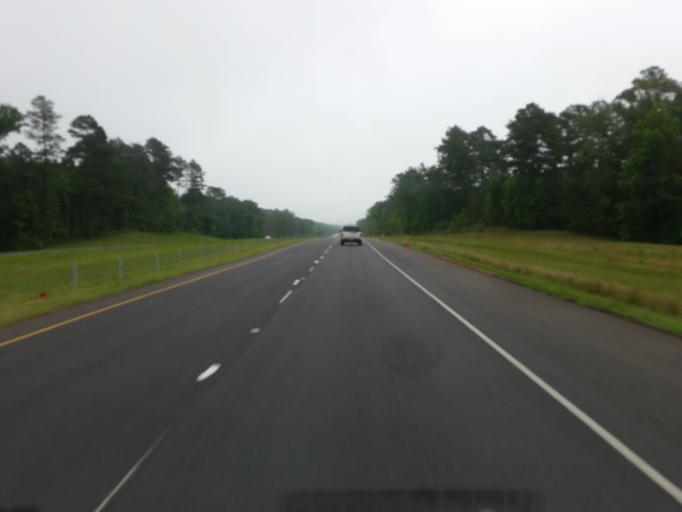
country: US
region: Louisiana
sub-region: Webster Parish
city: Minden
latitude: 32.5626
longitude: -93.1116
